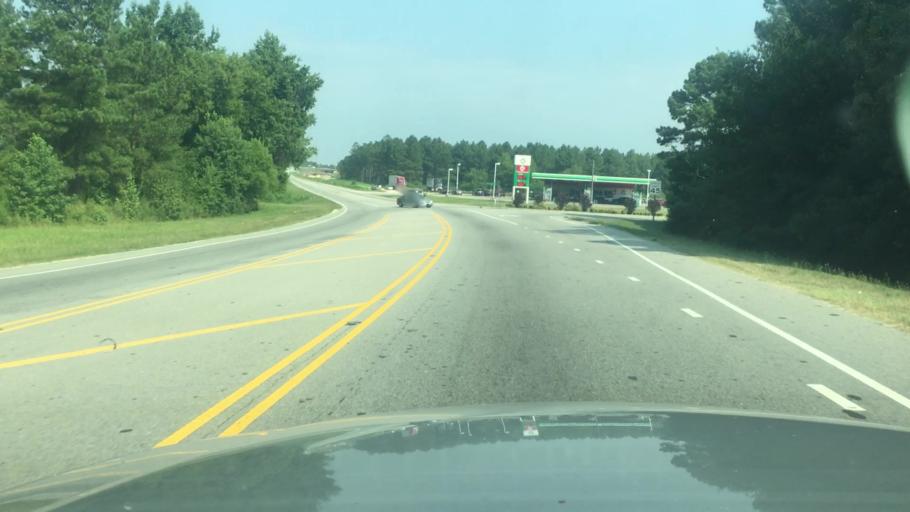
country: US
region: North Carolina
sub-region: Cumberland County
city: Hope Mills
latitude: 34.9403
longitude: -78.9241
